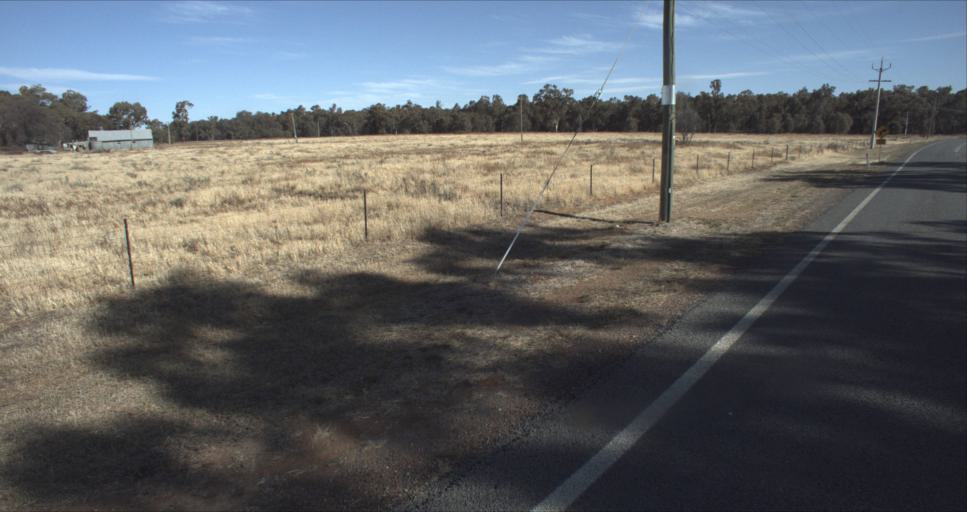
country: AU
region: New South Wales
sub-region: Leeton
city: Leeton
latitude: -34.6238
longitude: 146.3953
